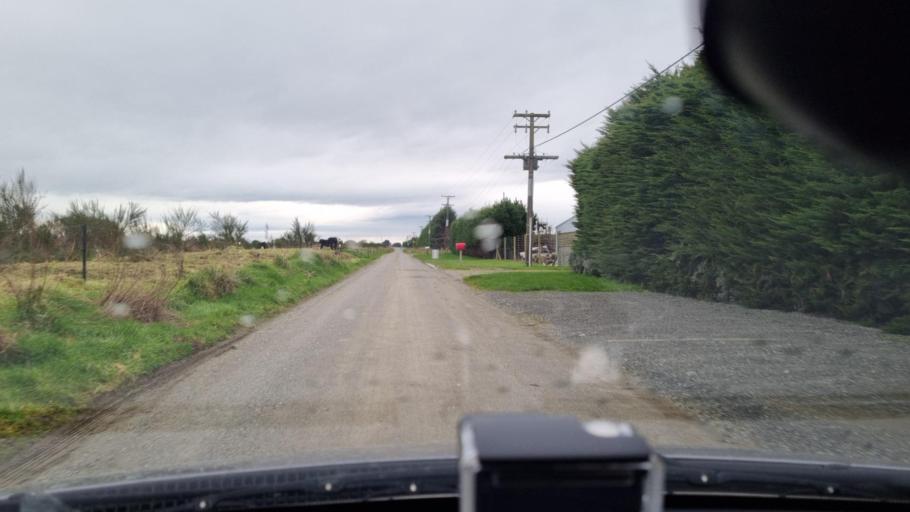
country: NZ
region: Southland
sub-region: Invercargill City
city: Invercargill
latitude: -46.3338
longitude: 168.3405
